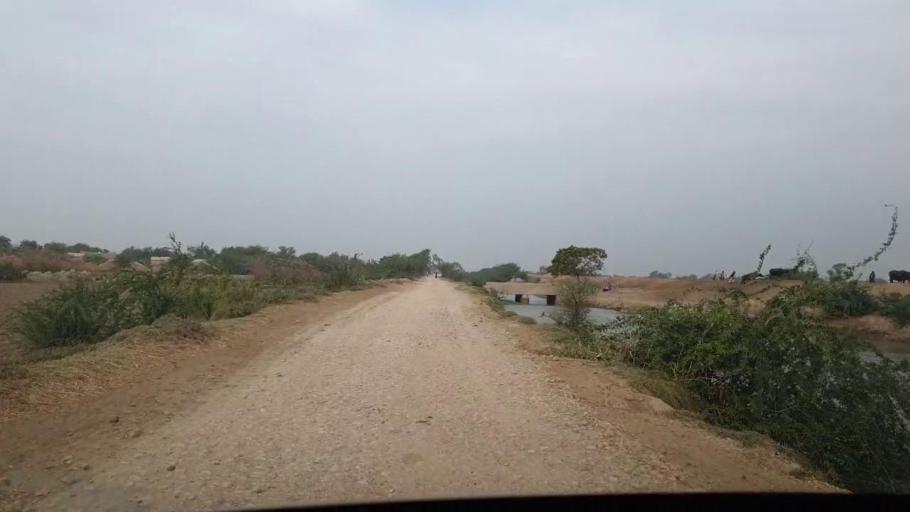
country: PK
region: Sindh
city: Chuhar Jamali
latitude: 24.4110
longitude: 67.9468
